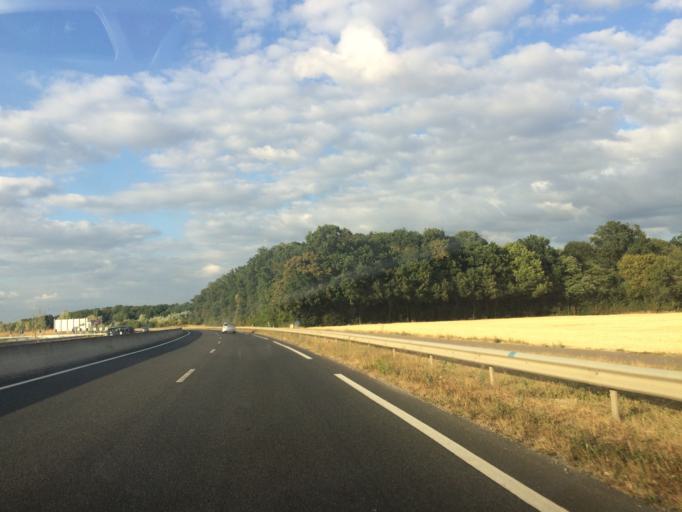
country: FR
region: Ile-de-France
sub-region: Departement de l'Essonne
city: Marolles-en-Hurepoix
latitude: 48.5802
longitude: 2.3030
